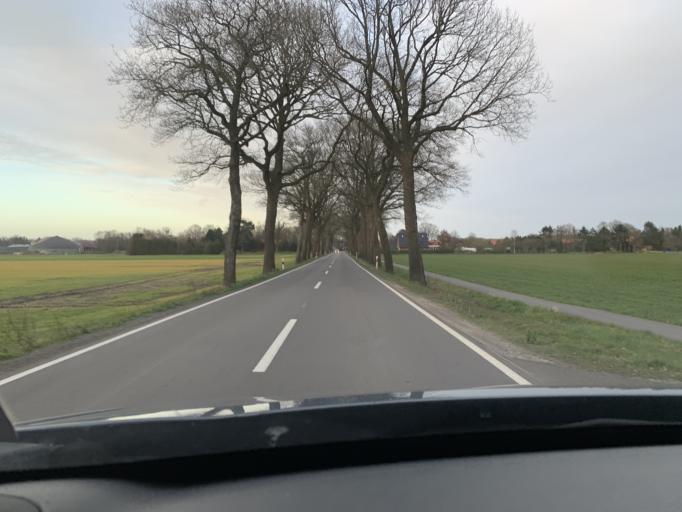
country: DE
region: Lower Saxony
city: Apen
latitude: 53.1896
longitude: 7.8618
